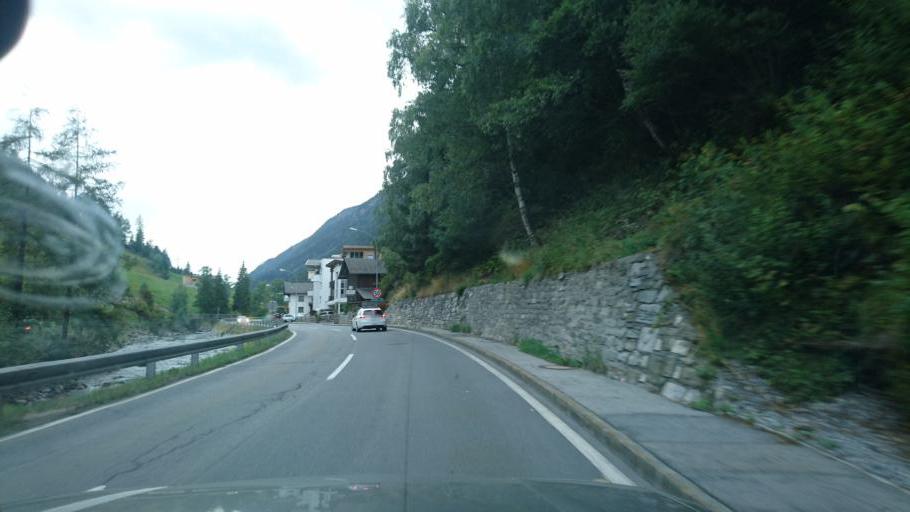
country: AT
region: Tyrol
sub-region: Politischer Bezirk Landeck
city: Kappl
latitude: 47.0504
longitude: 10.3502
